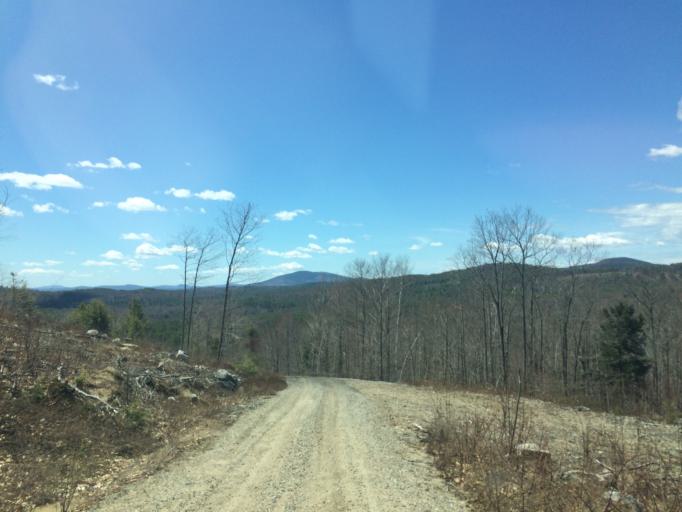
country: US
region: Maine
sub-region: Oxford County
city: Porter
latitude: 43.8503
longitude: -70.9169
